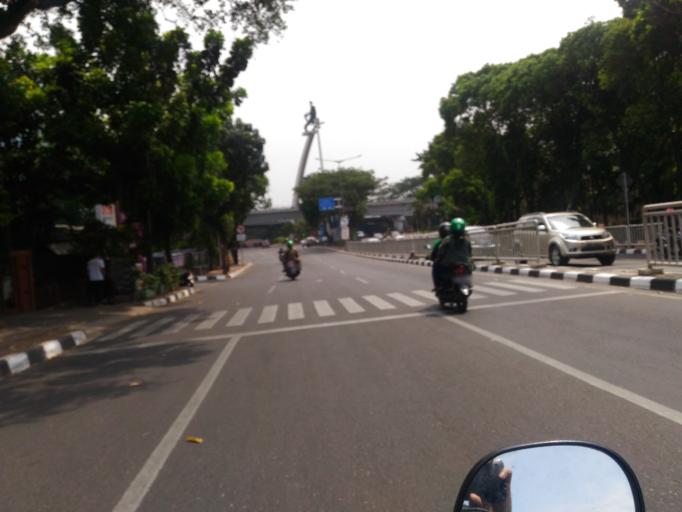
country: ID
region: Jakarta Raya
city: Jakarta
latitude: -6.2418
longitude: 106.8444
